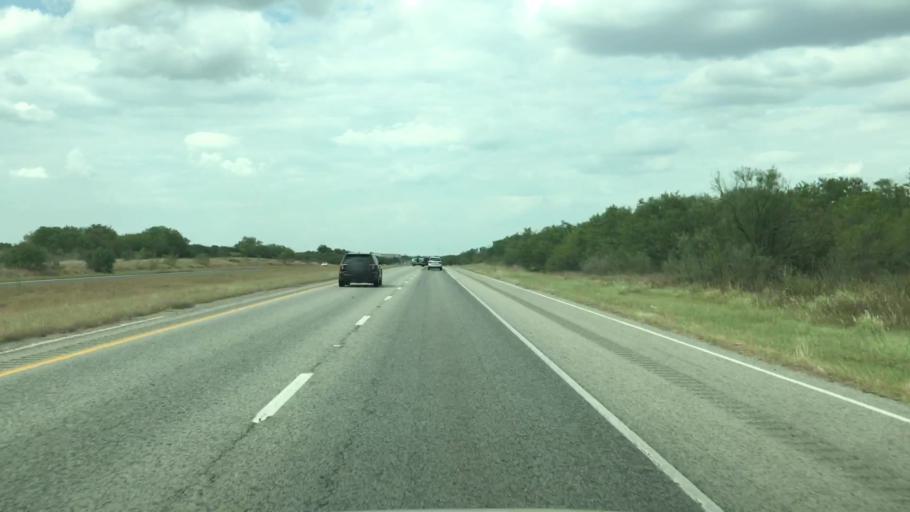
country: US
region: Texas
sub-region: Atascosa County
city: Pleasanton
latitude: 29.0715
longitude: -98.4328
